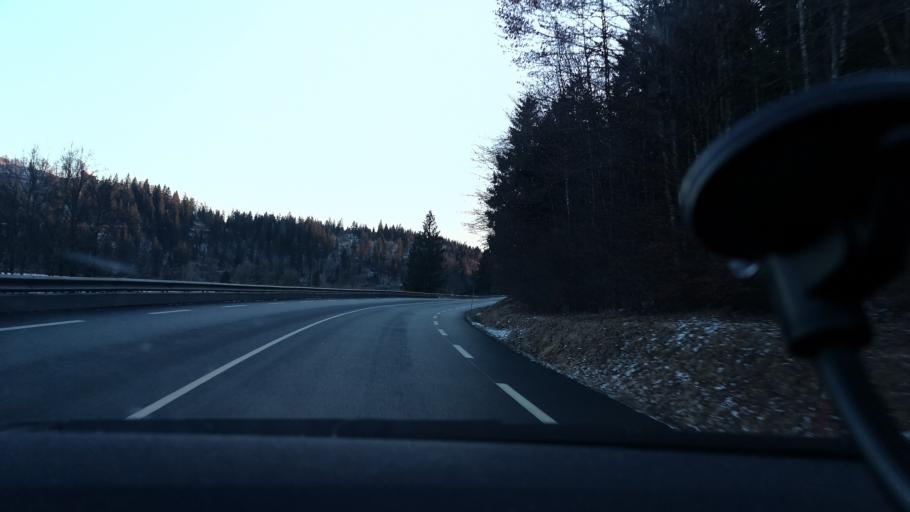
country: FR
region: Franche-Comte
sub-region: Departement du Doubs
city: La Cluse-et-Mijoux
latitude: 46.8782
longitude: 6.3671
